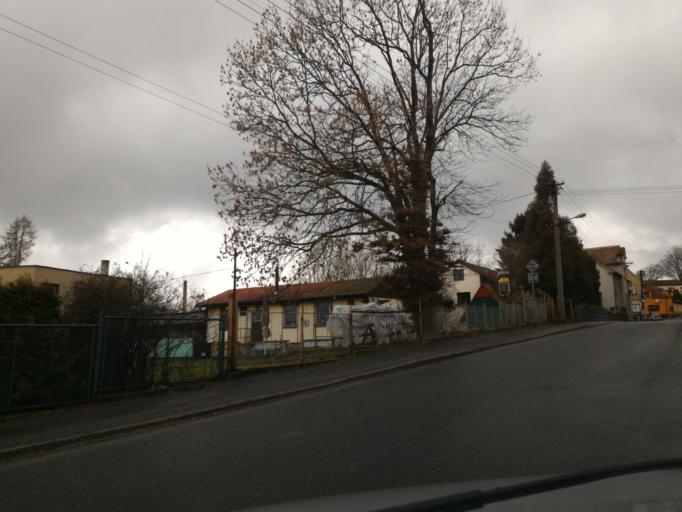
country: CZ
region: Liberecky
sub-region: Okres Liberec
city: Frydlant
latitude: 50.9234
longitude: 15.0761
